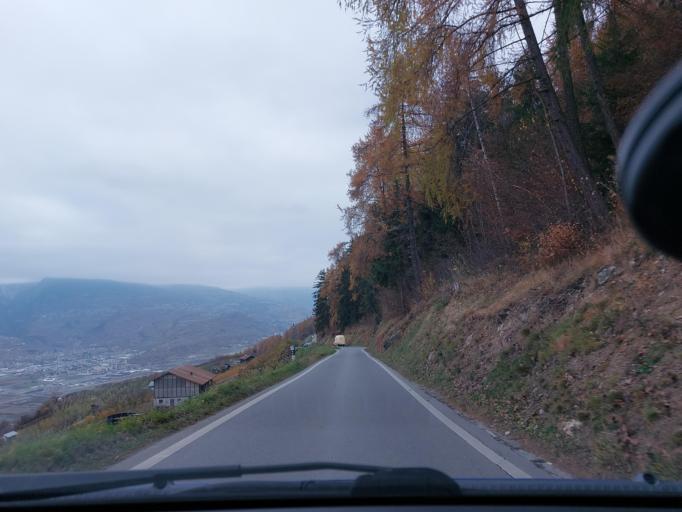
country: CH
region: Valais
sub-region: Conthey District
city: Ardon
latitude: 46.1875
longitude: 7.2778
